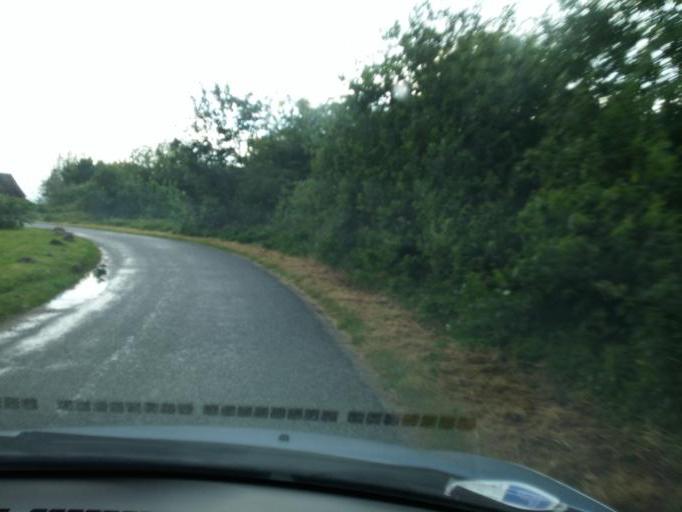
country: DK
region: South Denmark
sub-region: Kerteminde Kommune
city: Munkebo
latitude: 55.5179
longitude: 10.5730
